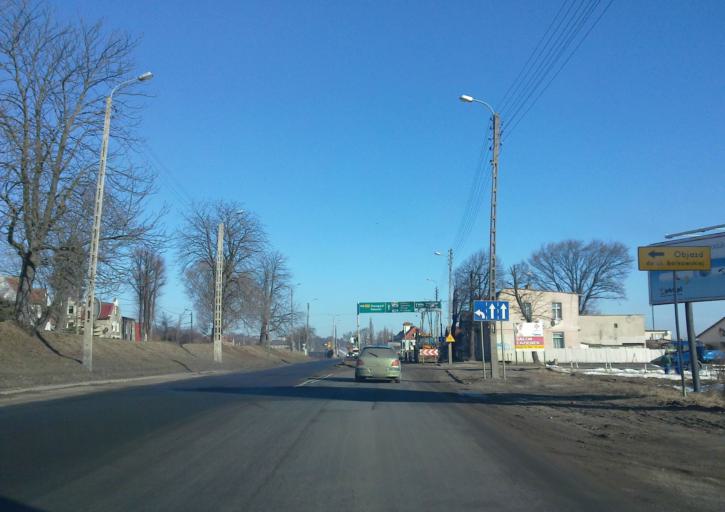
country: PL
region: Pomeranian Voivodeship
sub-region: Powiat gdanski
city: Rotmanka
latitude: 54.3082
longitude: 18.6299
